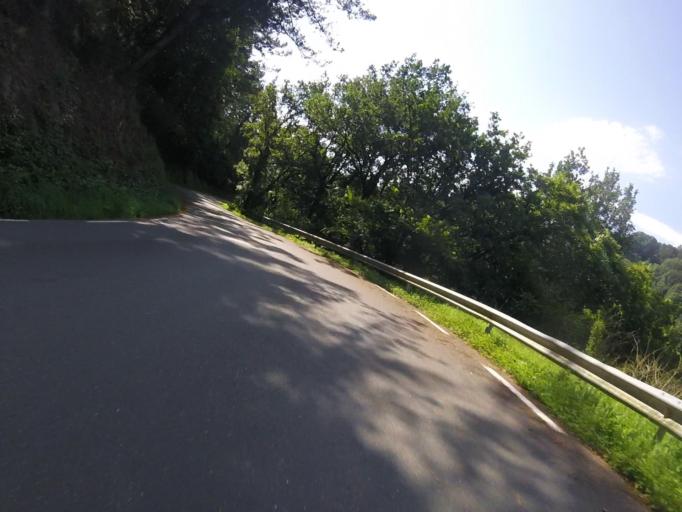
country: ES
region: Basque Country
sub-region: Provincia de Guipuzcoa
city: Hernialde
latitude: 43.1641
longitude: -2.0847
